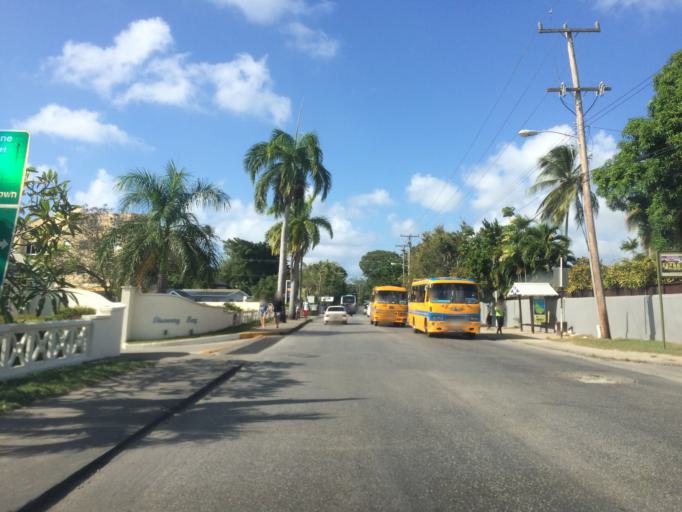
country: BB
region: Saint James
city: Holetown
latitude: 13.1880
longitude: -59.6364
